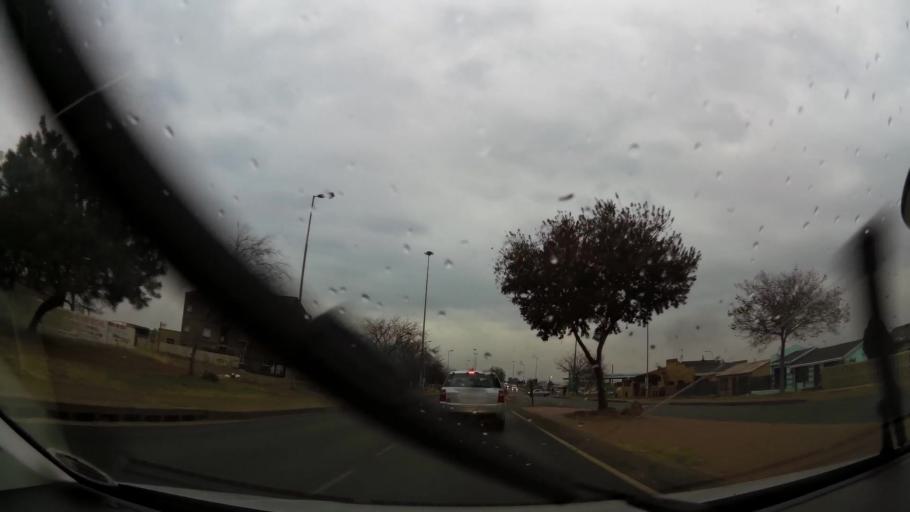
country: ZA
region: Gauteng
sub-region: City of Johannesburg Metropolitan Municipality
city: Soweto
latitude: -26.2567
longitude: 27.8553
